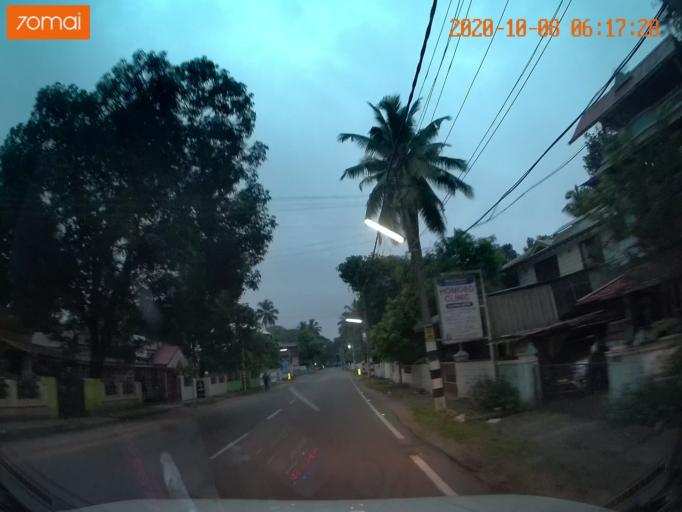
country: IN
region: Kerala
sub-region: Thrissur District
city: Trichur
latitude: 10.5118
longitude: 76.2573
